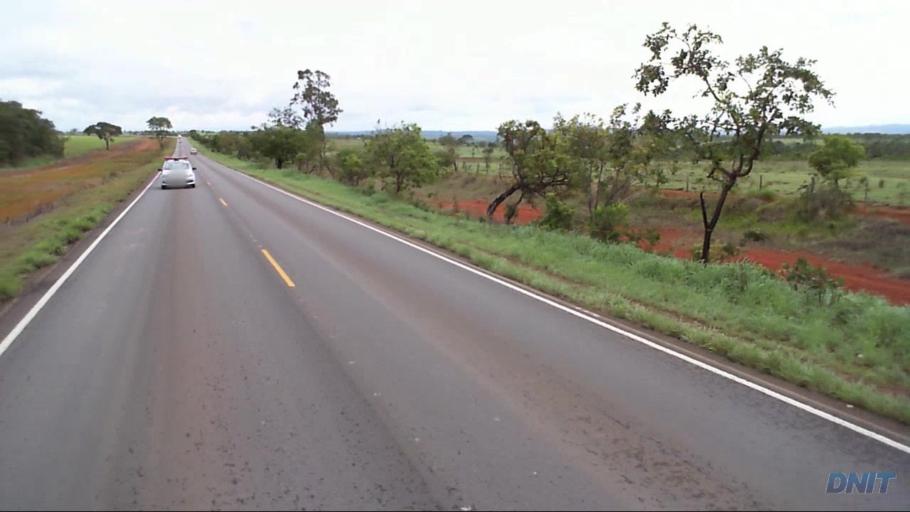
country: BR
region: Goias
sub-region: Padre Bernardo
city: Padre Bernardo
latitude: -15.3155
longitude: -48.2286
